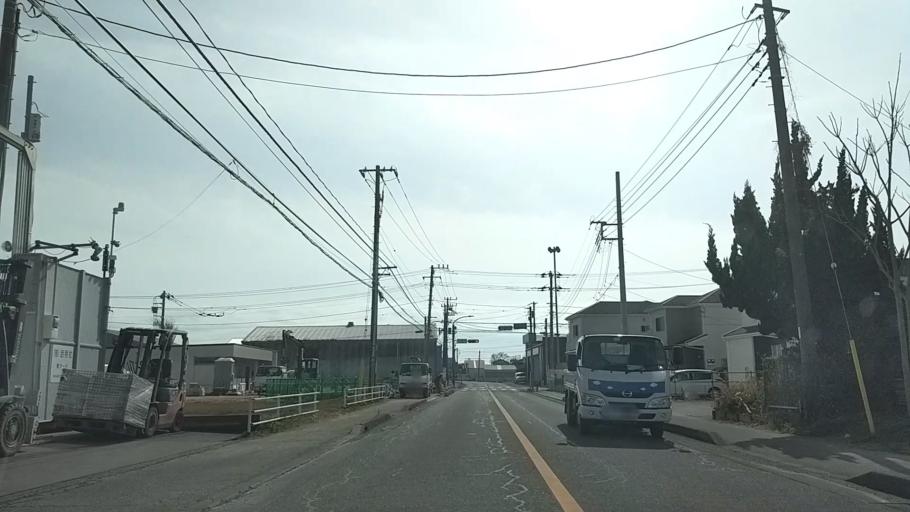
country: JP
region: Kanagawa
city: Chigasaki
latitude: 35.3583
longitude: 139.3845
